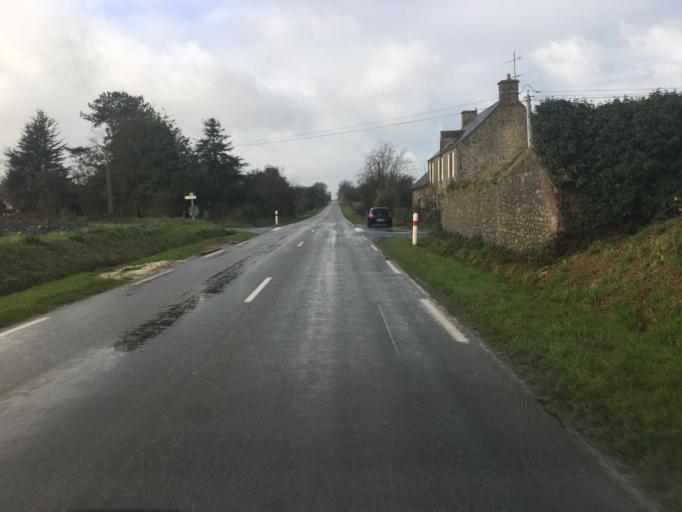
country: FR
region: Lower Normandy
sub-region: Departement de la Manche
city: Saint-Pierre-Eglise
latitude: 49.6692
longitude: -1.3632
